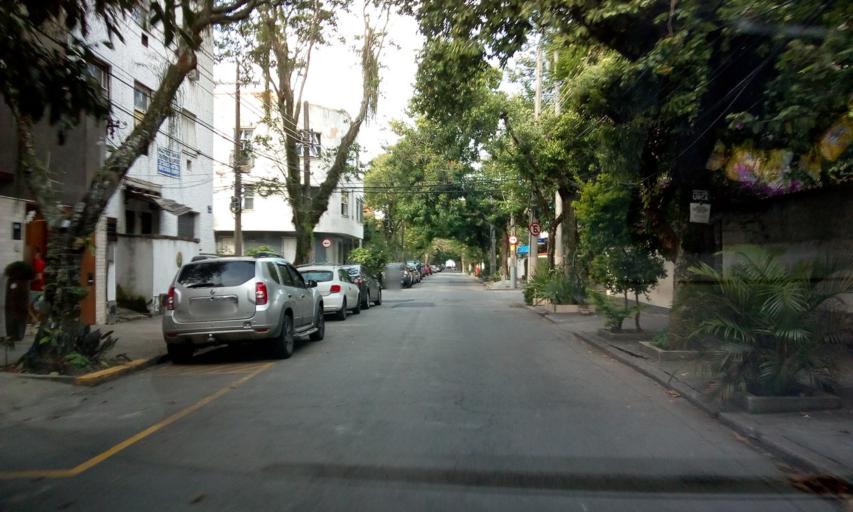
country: BR
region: Rio de Janeiro
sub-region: Rio De Janeiro
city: Rio de Janeiro
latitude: -22.9467
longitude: -43.1621
